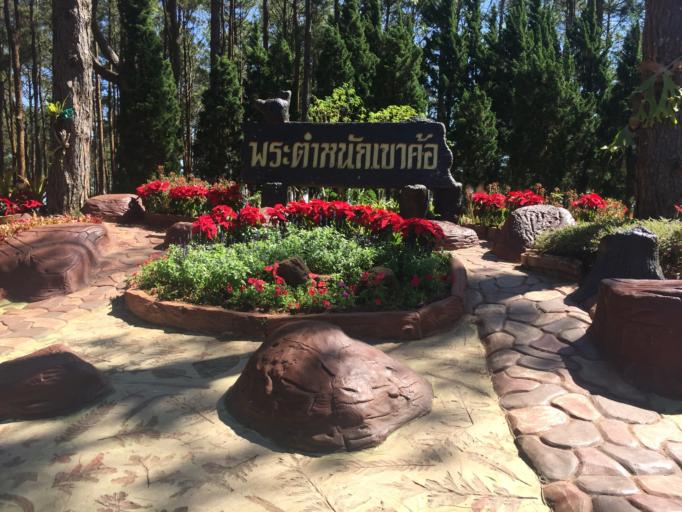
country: TH
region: Phetchabun
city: Khao Kho
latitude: 16.5523
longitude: 100.9758
